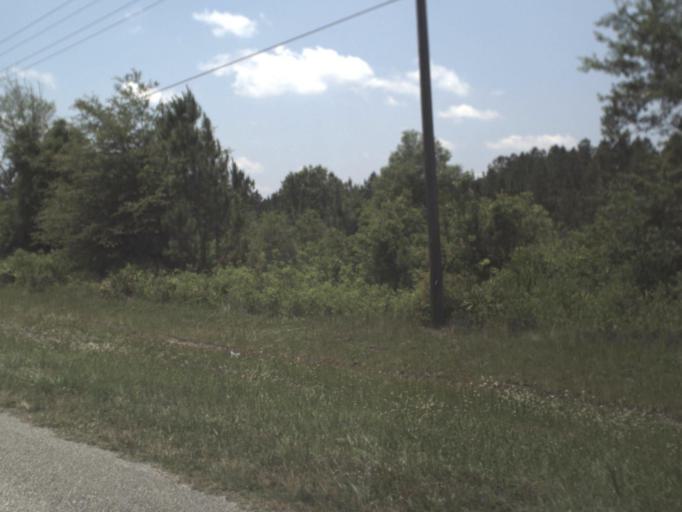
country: US
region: Florida
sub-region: Bradford County
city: Starke
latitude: 29.8981
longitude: -82.1375
